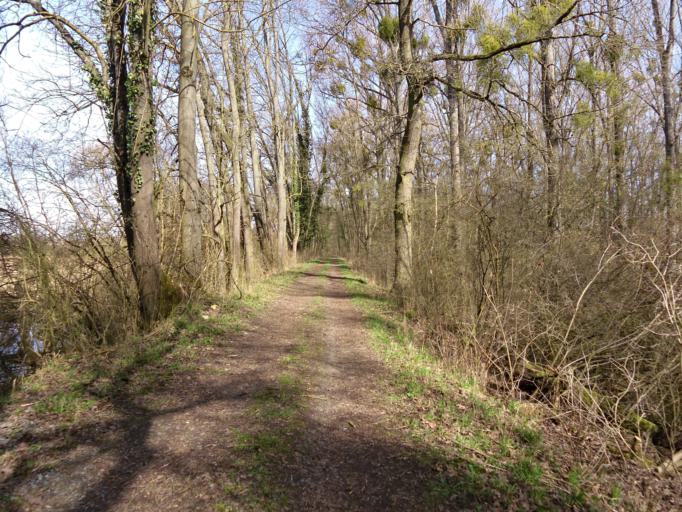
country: DE
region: Hesse
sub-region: Regierungsbezirk Darmstadt
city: Stockstadt am Rhein
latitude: 49.8189
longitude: 8.4187
